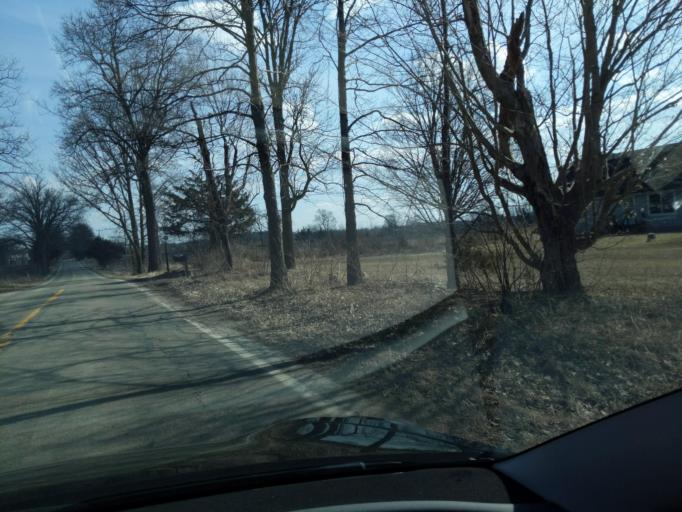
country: US
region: Michigan
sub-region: Ingham County
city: Stockbridge
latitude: 42.4458
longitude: -84.0643
